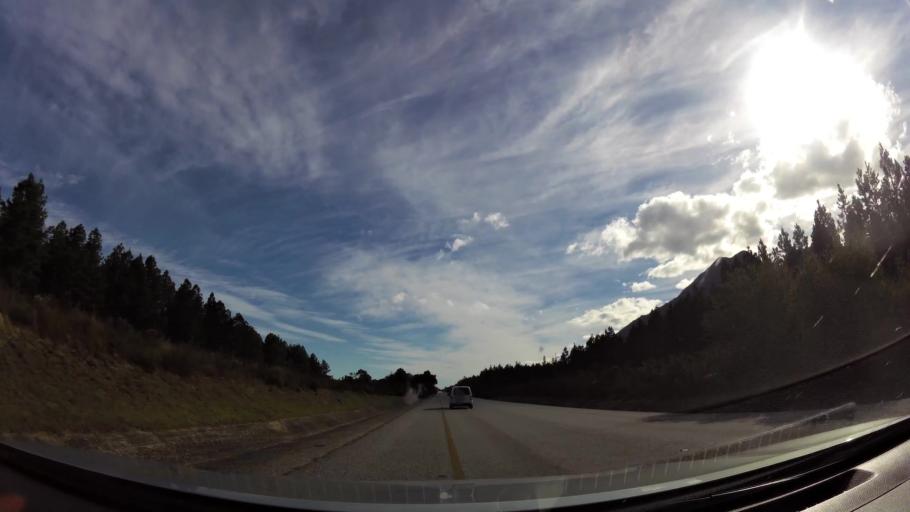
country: ZA
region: Eastern Cape
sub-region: Cacadu District Municipality
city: Kareedouw
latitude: -33.9913
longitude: 24.1265
